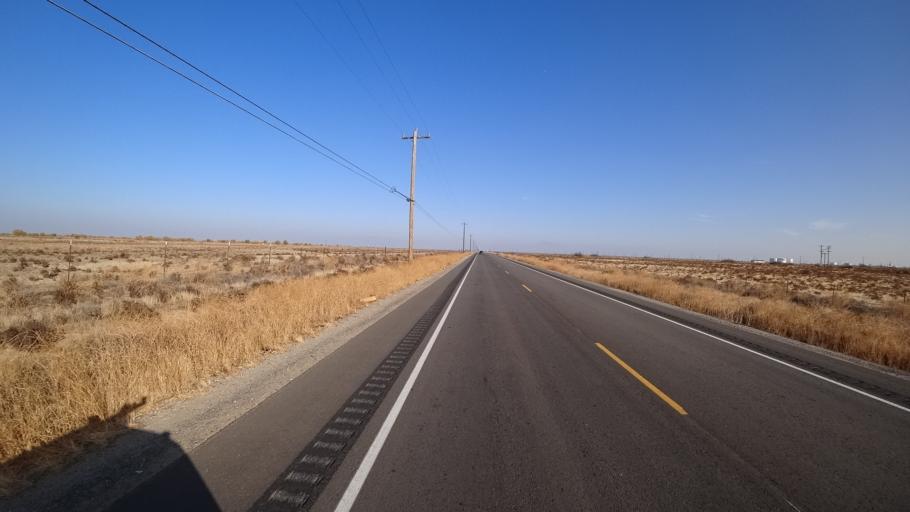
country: US
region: California
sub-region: Kern County
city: Rosedale
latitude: 35.2961
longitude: -119.2230
